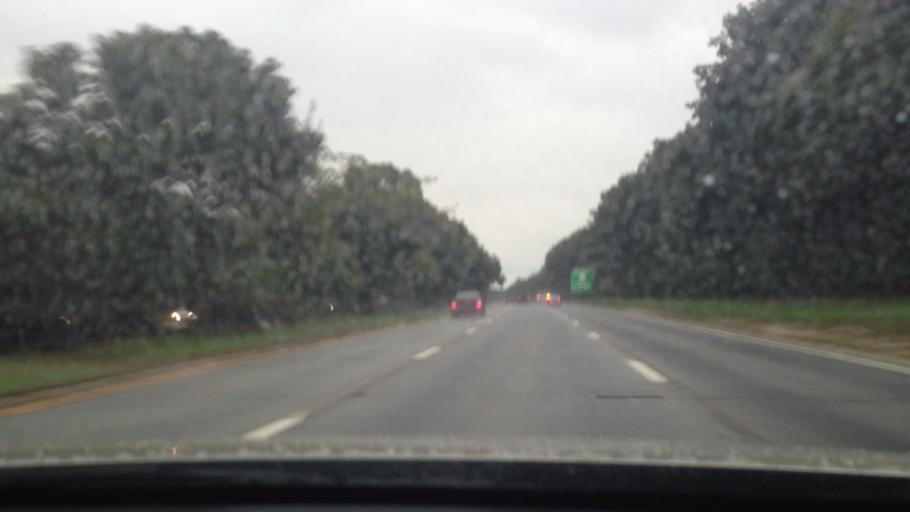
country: US
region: New York
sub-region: Suffolk County
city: Islip
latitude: 40.7548
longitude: -73.2244
